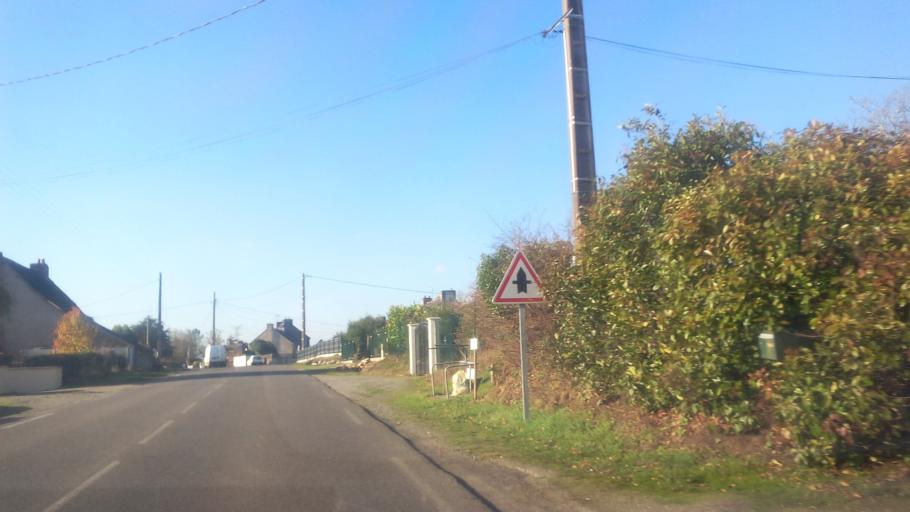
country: FR
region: Brittany
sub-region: Departement du Morbihan
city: Saint-Perreux
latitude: 47.6785
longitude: -2.1230
